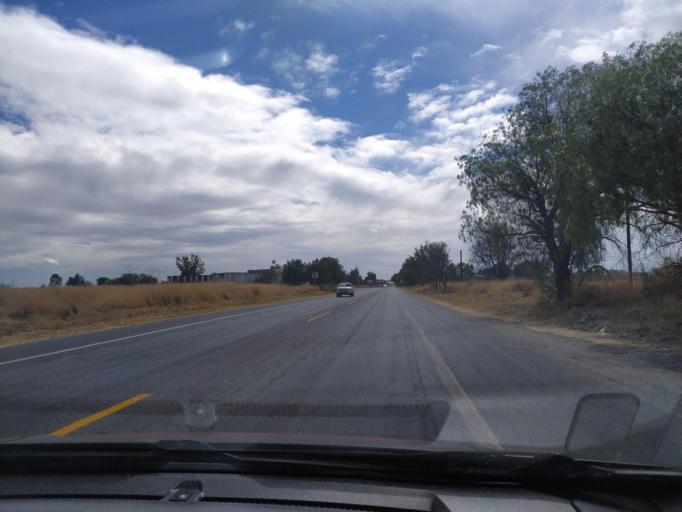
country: LA
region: Oudomxai
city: Muang La
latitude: 21.0189
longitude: 101.8269
